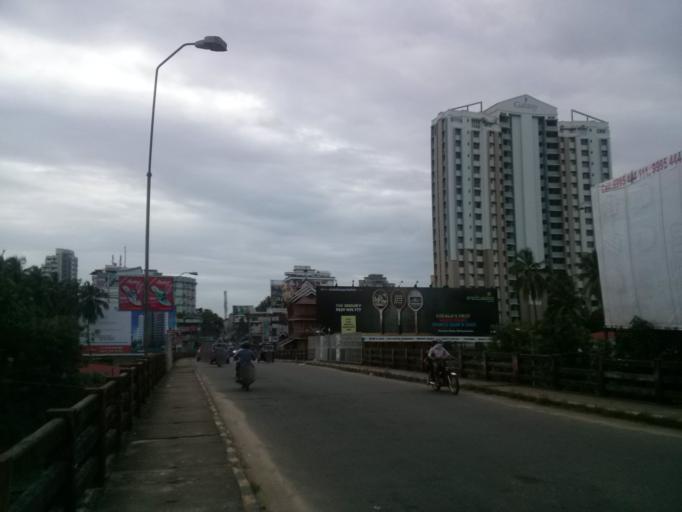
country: IN
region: Kerala
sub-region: Kozhikode
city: Kozhikode
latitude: 11.2566
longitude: 75.7781
